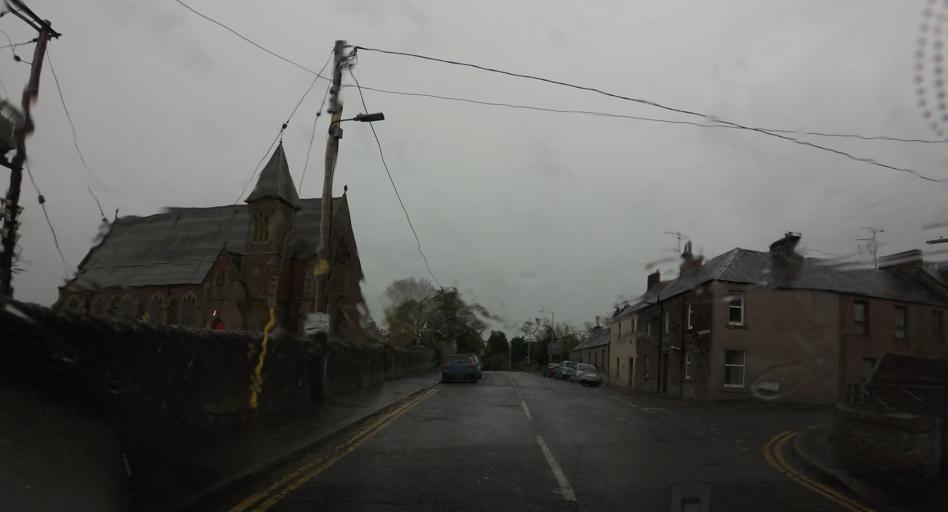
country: GB
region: Scotland
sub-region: Perth and Kinross
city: Coupar Angus
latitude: 56.5440
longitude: -3.2657
